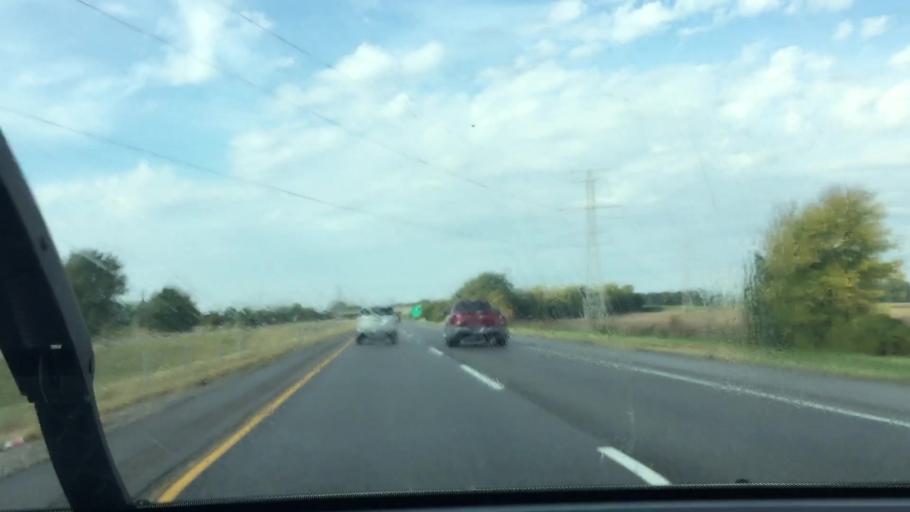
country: US
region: Illinois
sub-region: Whiteside County
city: Rock Falls
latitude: 41.7698
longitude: -89.5935
